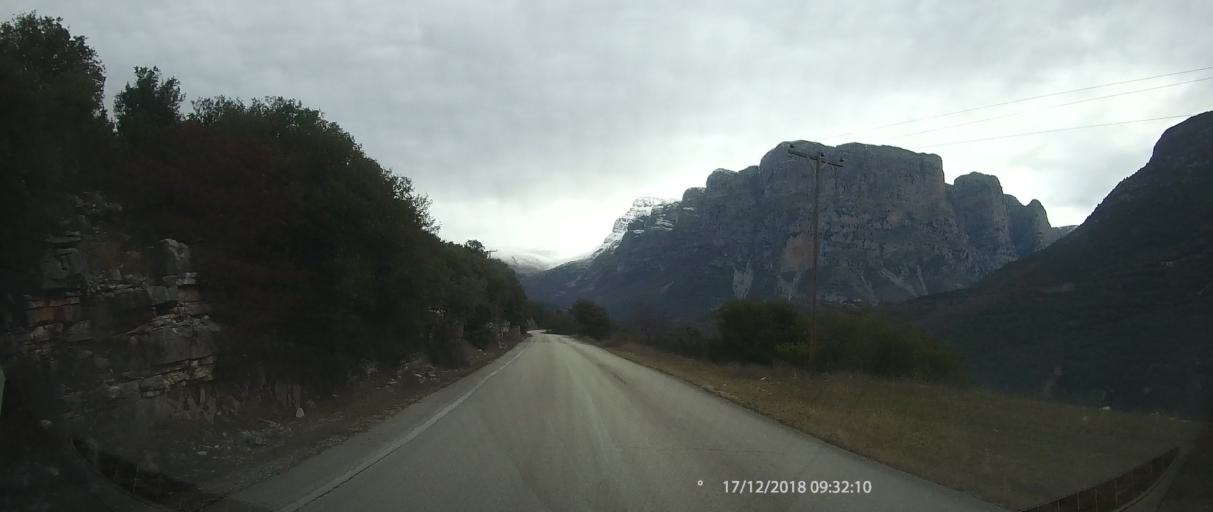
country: GR
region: Epirus
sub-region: Nomos Ioanninon
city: Kalpaki
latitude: 39.9509
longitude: 20.6910
